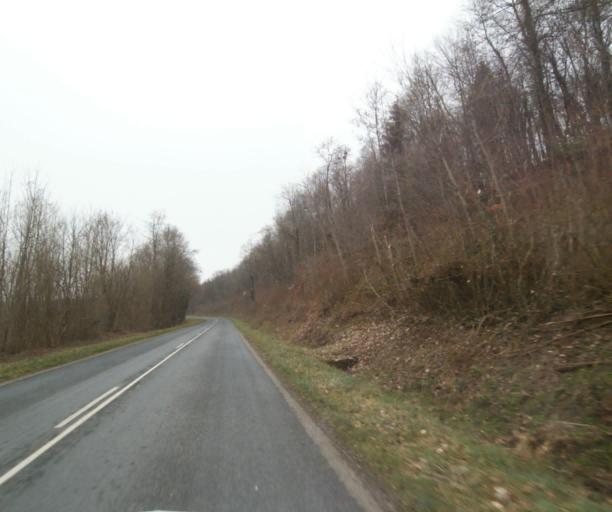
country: FR
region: Champagne-Ardenne
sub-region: Departement de la Haute-Marne
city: Bienville
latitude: 48.5731
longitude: 5.0377
